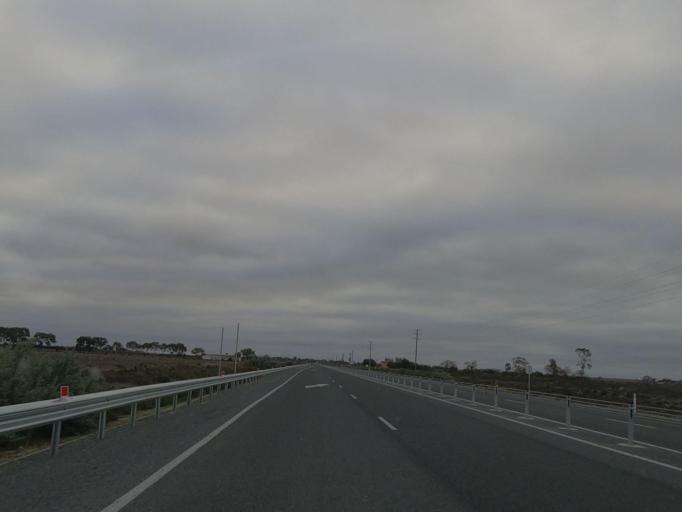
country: AU
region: Victoria
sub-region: Swan Hill
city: Swan Hill
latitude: -35.4771
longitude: 143.6831
